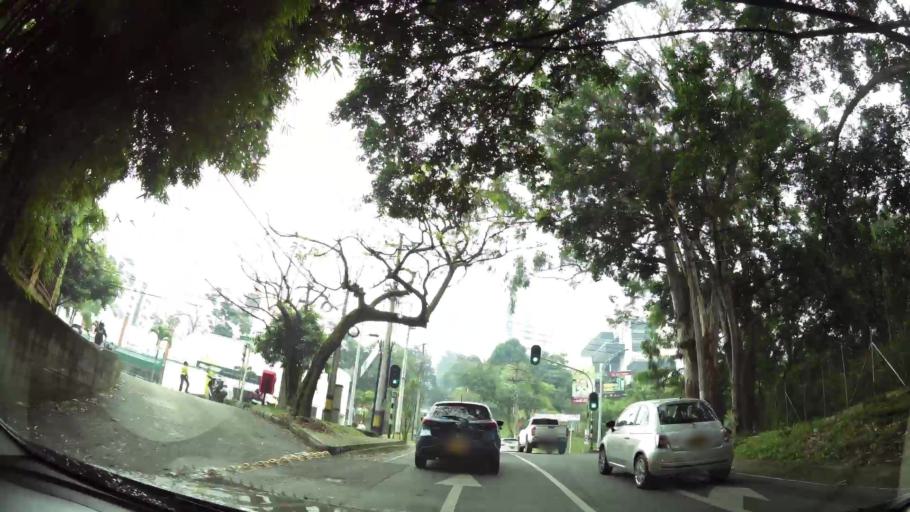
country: CO
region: Antioquia
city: Envigado
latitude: 6.1962
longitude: -75.5662
